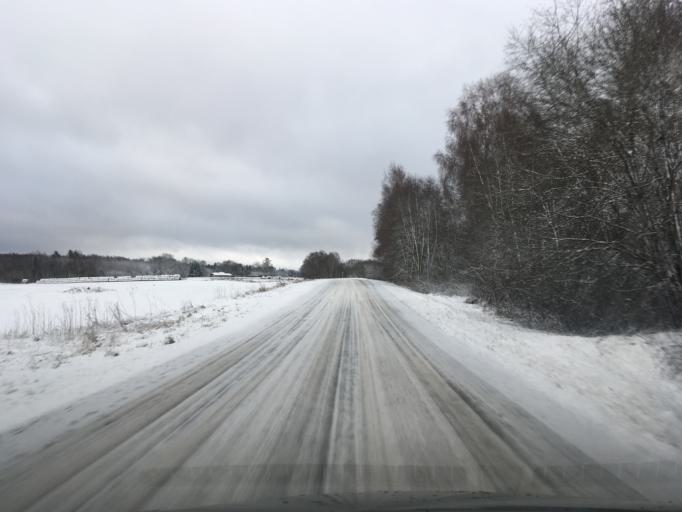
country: EE
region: Harju
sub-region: Raasiku vald
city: Raasiku
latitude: 59.2542
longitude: 25.1327
